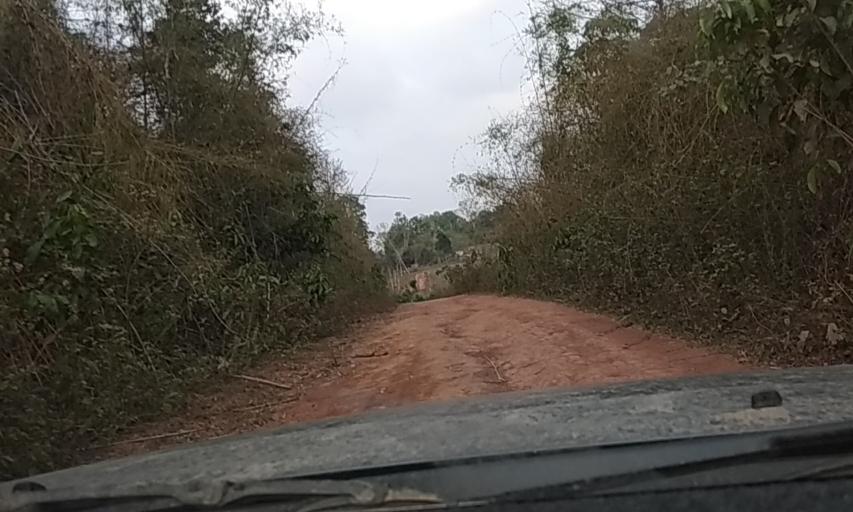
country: TH
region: Nan
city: Mae Charim
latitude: 18.4559
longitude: 101.1942
